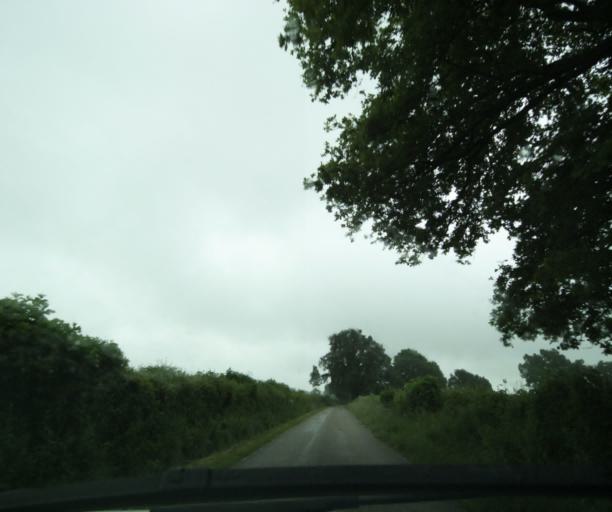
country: FR
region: Bourgogne
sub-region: Departement de Saone-et-Loire
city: Charolles
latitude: 46.3668
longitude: 4.2106
